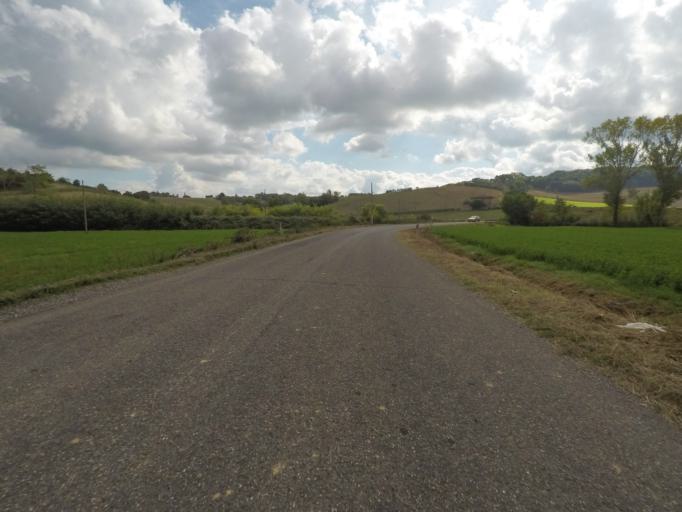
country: IT
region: Tuscany
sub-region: Provincia di Siena
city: Torrita di Siena
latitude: 43.1608
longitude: 11.7729
